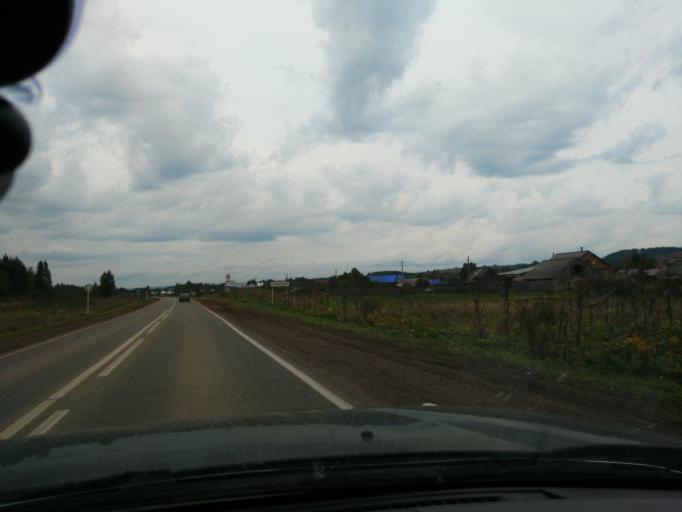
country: RU
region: Perm
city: Chernushka
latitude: 56.7273
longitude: 56.1784
